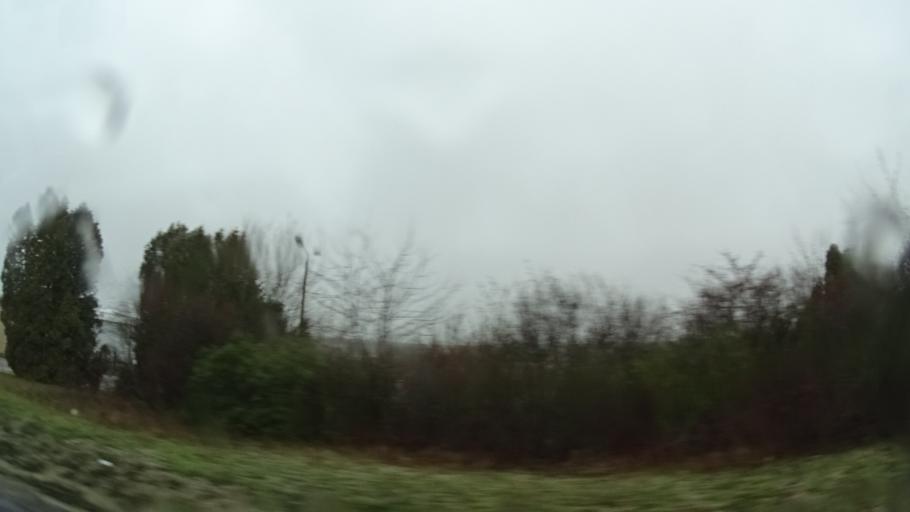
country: DE
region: Thuringia
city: Eisfeld
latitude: 50.4424
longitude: 10.9107
